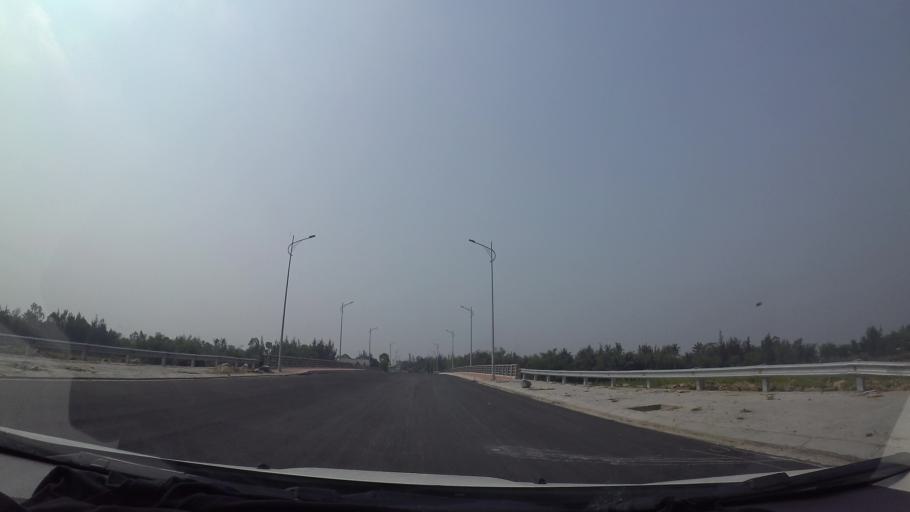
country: VN
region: Da Nang
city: Ngu Hanh Son
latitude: 15.9946
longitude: 108.2467
